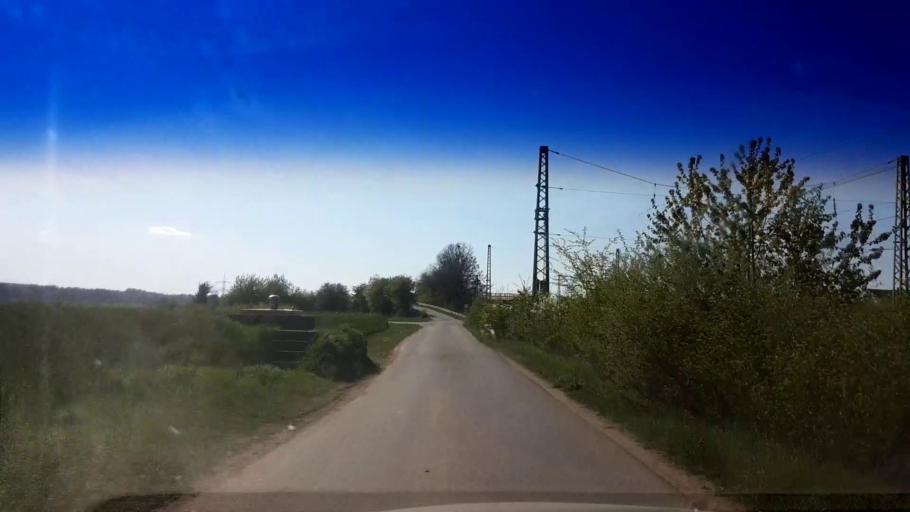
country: DE
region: Bavaria
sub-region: Upper Franconia
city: Oberhaid
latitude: 49.9292
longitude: 10.8261
